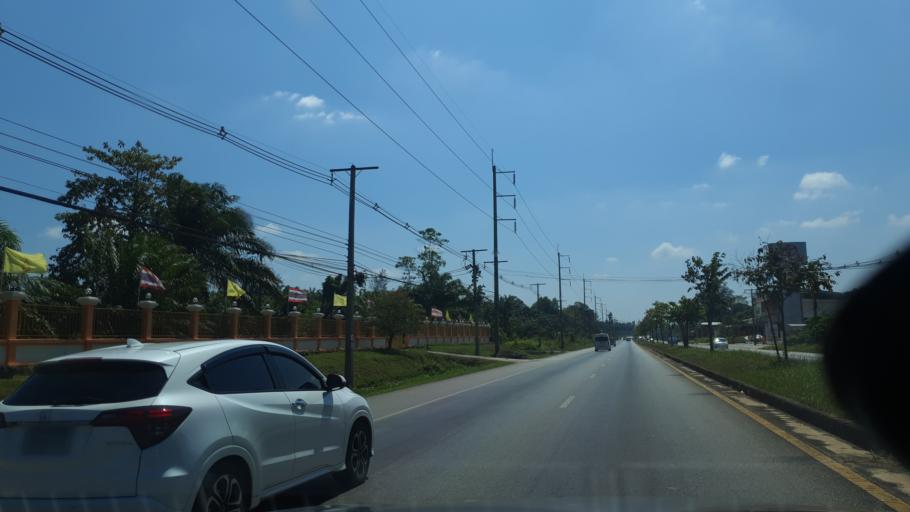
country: TH
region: Krabi
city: Khlong Thom
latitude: 7.9765
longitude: 99.1391
